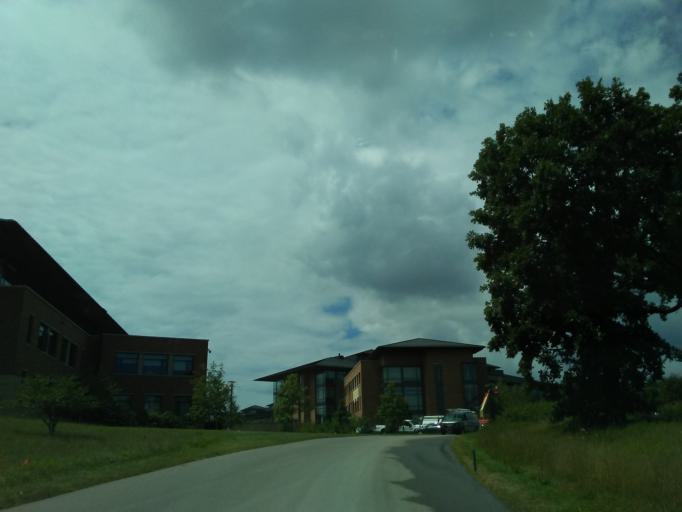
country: US
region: Wisconsin
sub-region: Dane County
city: Verona
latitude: 42.9929
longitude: -89.5641
